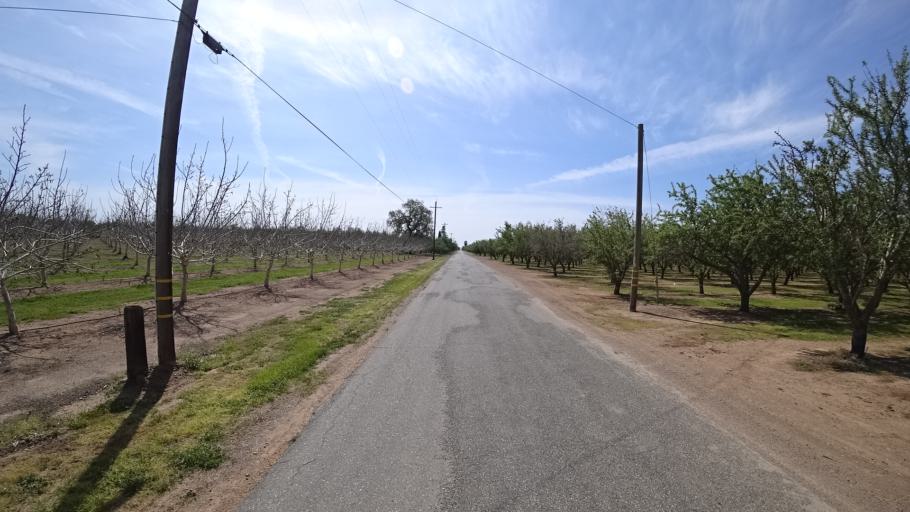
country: US
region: California
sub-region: Glenn County
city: Hamilton City
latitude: 39.8025
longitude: -122.0665
